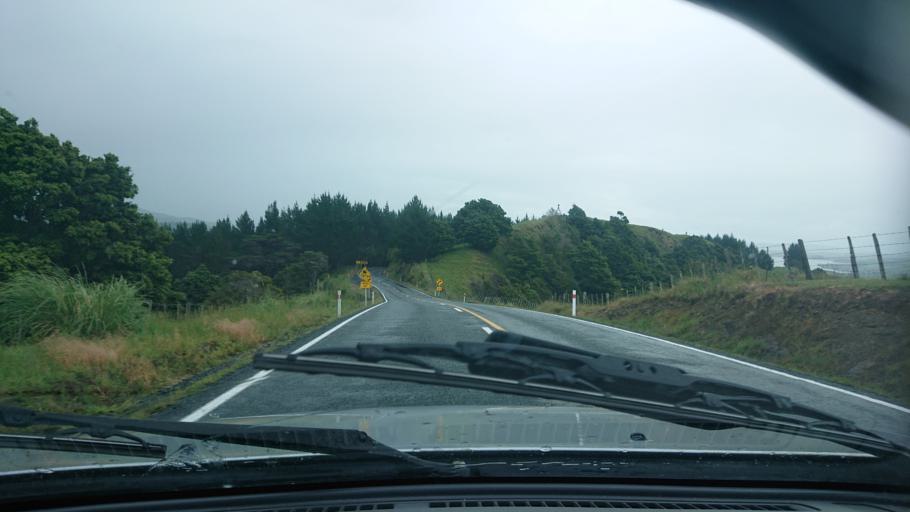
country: NZ
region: Auckland
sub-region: Auckland
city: Wellsford
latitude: -36.3583
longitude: 174.4683
